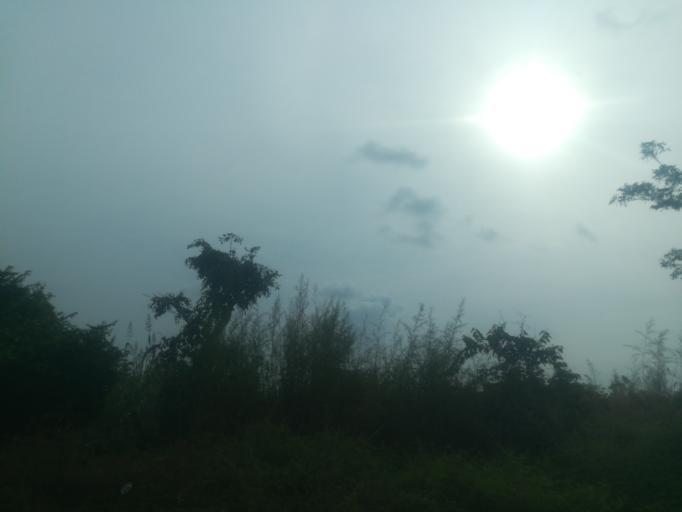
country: NG
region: Ogun
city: Ayetoro
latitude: 7.2881
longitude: 3.0838
